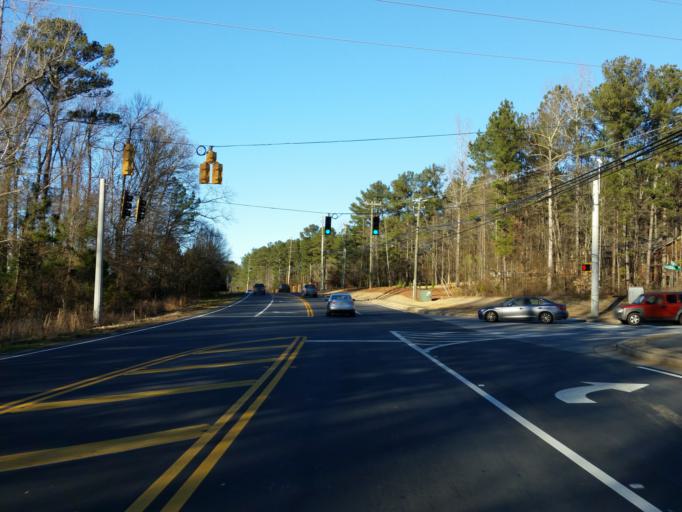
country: US
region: Georgia
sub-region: Cherokee County
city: Woodstock
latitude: 34.0984
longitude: -84.4707
